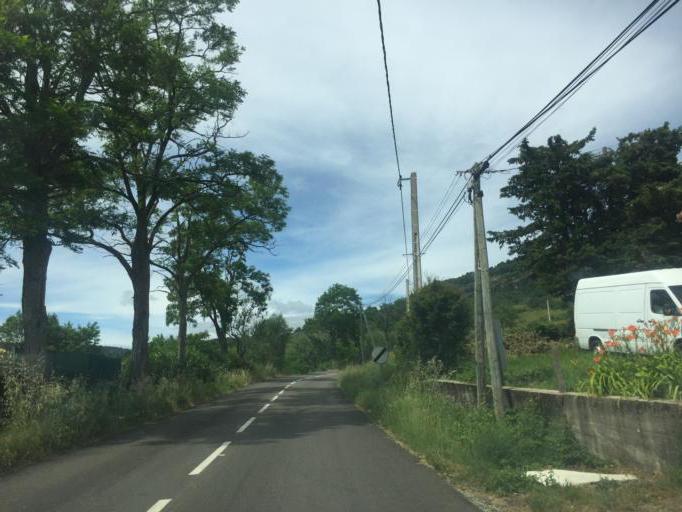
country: FR
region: Rhone-Alpes
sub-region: Departement de l'Ardeche
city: Villeneuve-de-Berg
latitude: 44.5985
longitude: 4.5370
